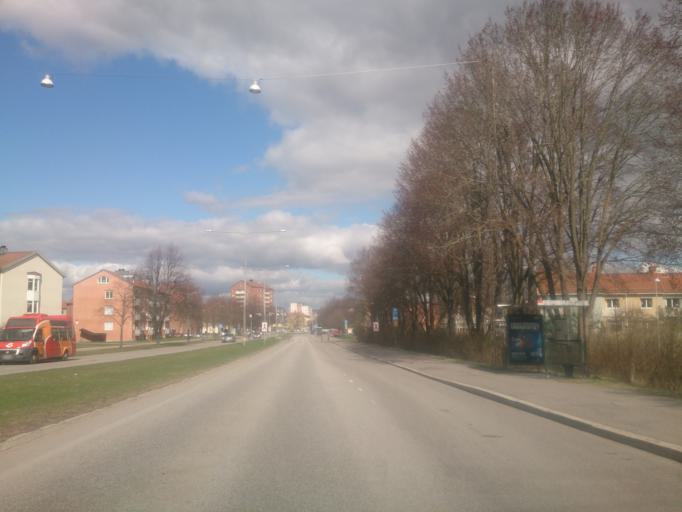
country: SE
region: OEstergoetland
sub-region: Norrkopings Kommun
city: Norrkoping
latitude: 58.5775
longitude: 16.1810
